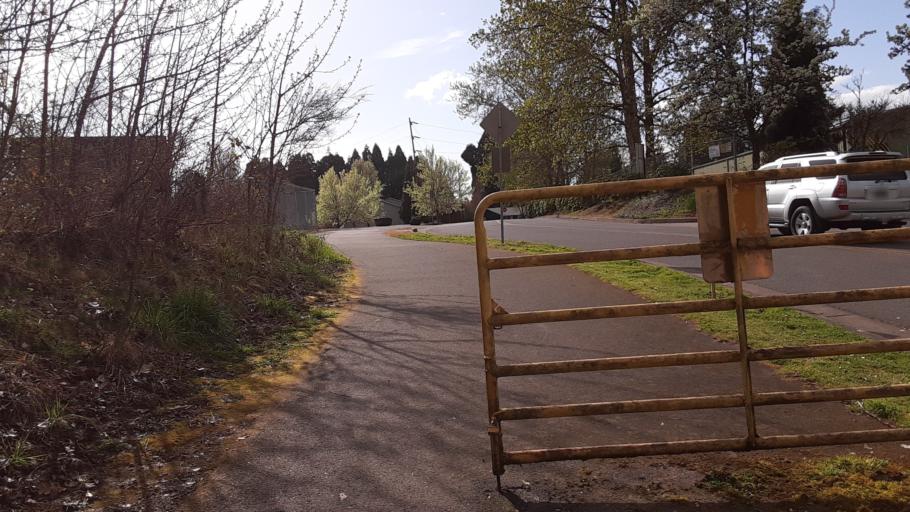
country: US
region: Oregon
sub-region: Benton County
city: Corvallis
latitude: 44.5507
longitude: -123.2552
